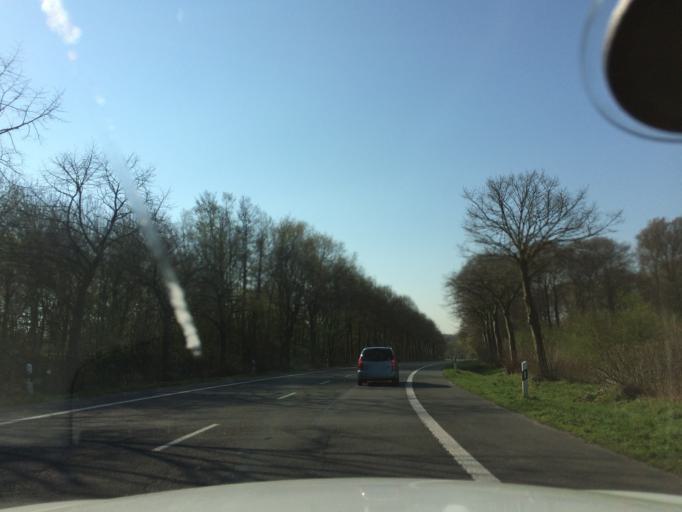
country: DE
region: North Rhine-Westphalia
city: Marl
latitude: 51.6150
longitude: 7.0848
